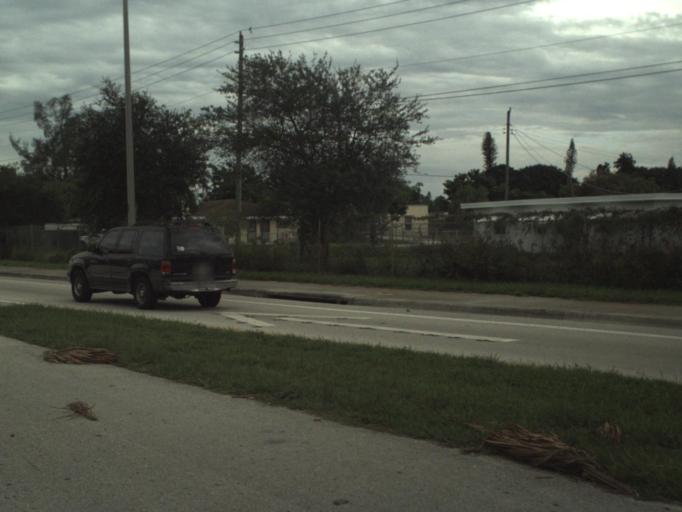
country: US
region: Florida
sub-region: Palm Beach County
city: Royal Palm Estates
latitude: 26.6784
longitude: -80.1242
